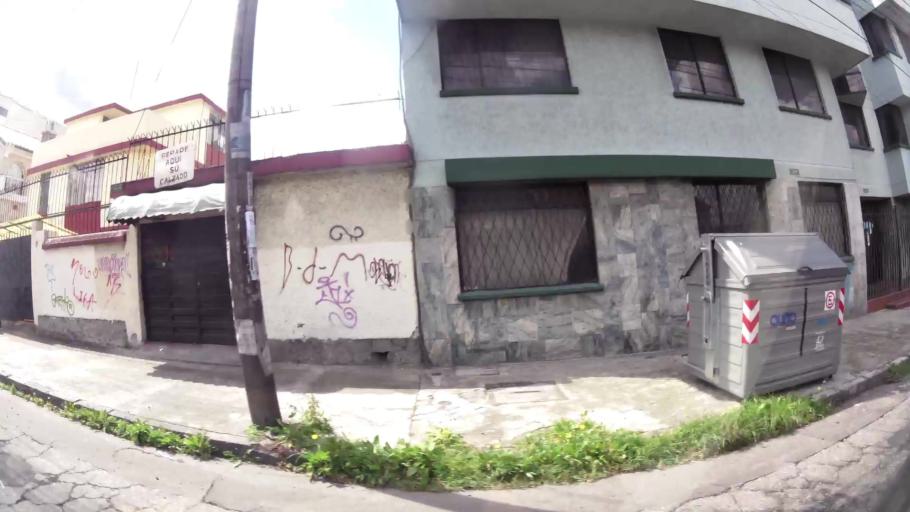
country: EC
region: Pichincha
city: Quito
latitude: -0.2033
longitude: -78.5034
